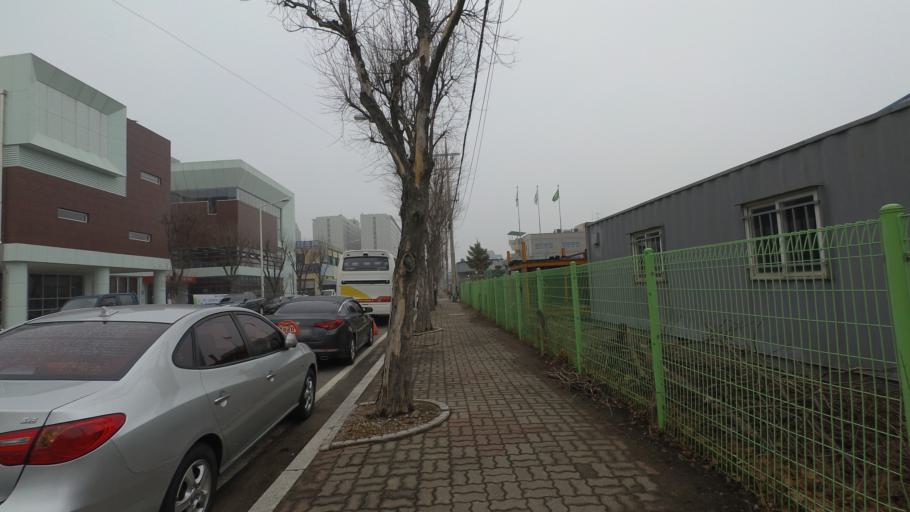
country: KR
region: Chungcheongnam-do
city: Tangjin
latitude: 36.9749
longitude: 126.8457
